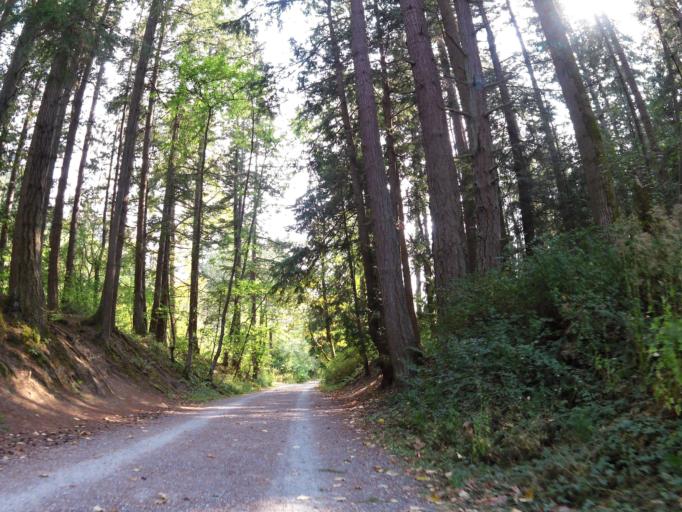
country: US
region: Washington
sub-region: Whatcom County
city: Bellingham
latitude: 48.7107
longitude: -122.4858
